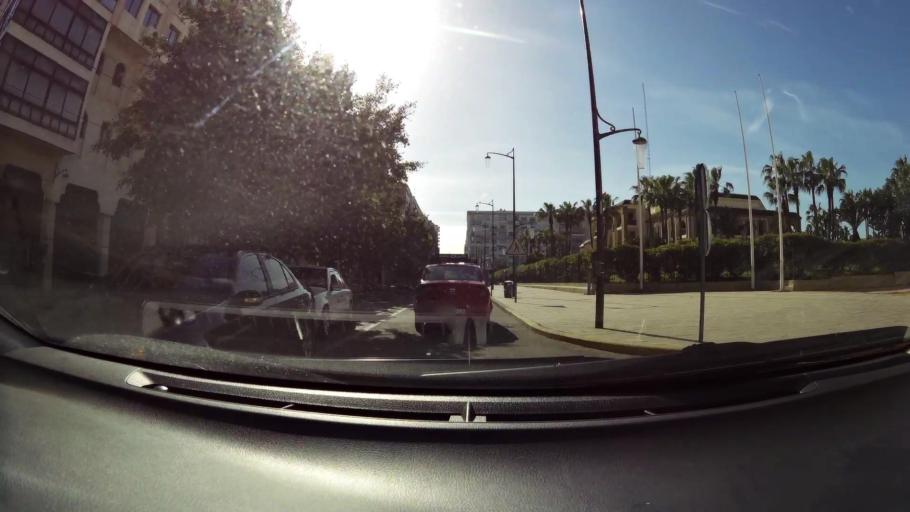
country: MA
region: Grand Casablanca
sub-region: Casablanca
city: Casablanca
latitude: 33.5925
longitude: -7.5964
